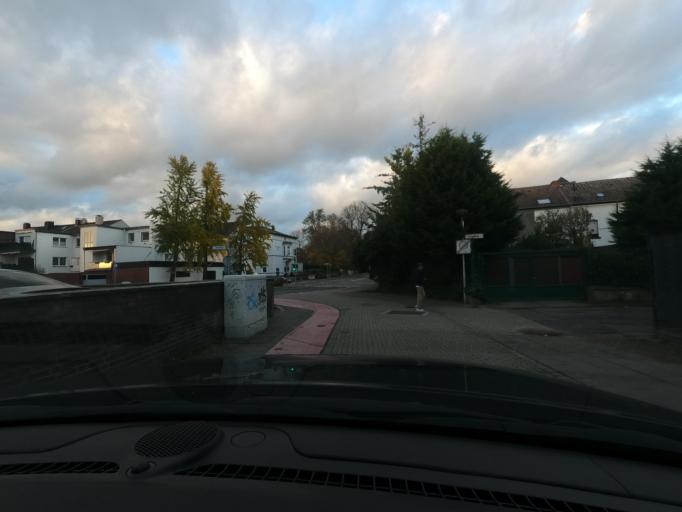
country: DE
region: North Rhine-Westphalia
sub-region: Regierungsbezirk Dusseldorf
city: Viersen
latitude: 51.2521
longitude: 6.3285
